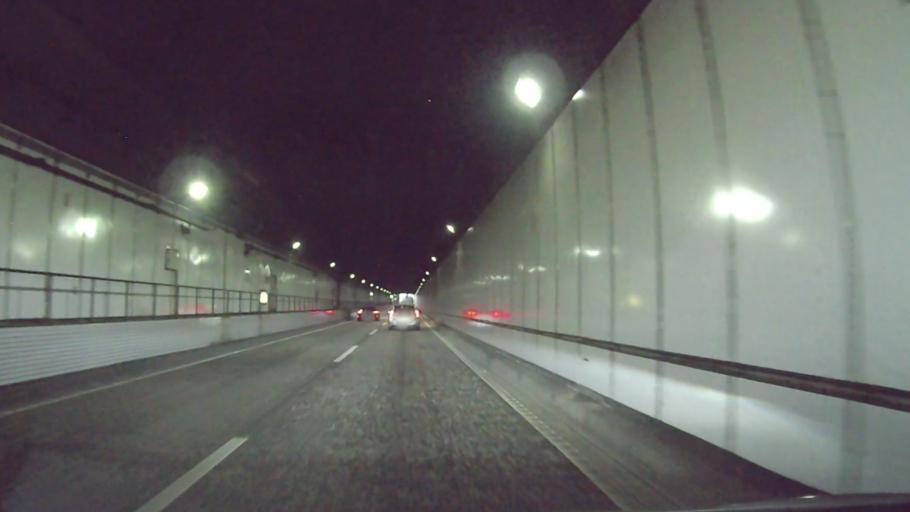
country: JP
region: Tokyo
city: Musashino
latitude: 35.7230
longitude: 139.6143
